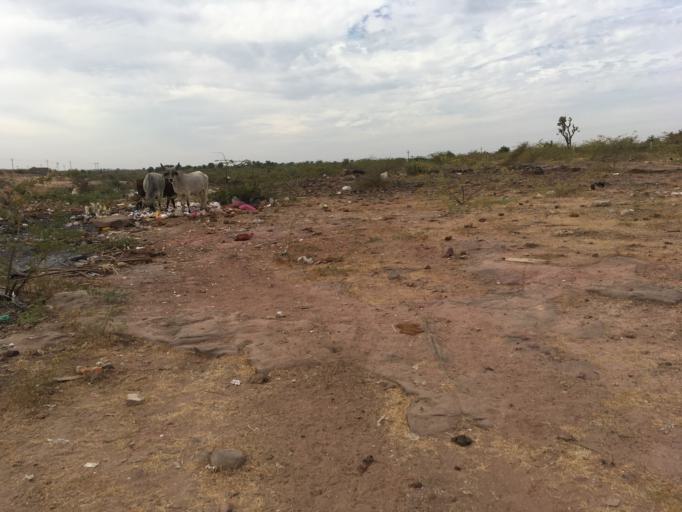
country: IN
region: Gujarat
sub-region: Kachchh
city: Bhuj
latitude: 23.2515
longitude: 69.6297
